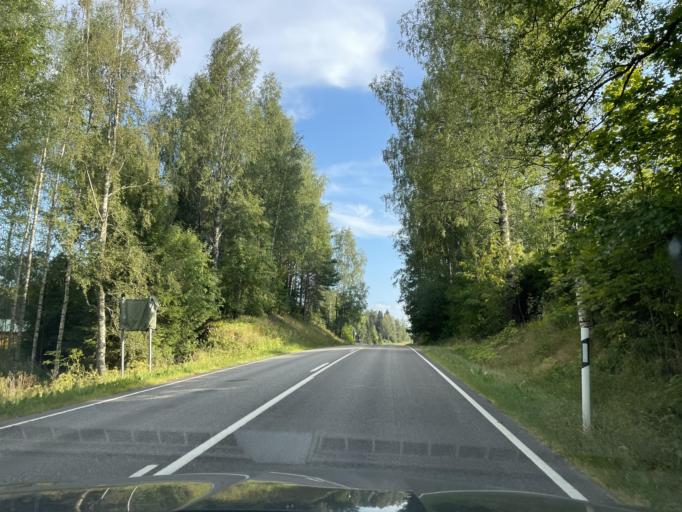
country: FI
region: Paijanne Tavastia
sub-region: Lahti
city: Auttoinen
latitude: 61.3015
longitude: 25.0887
